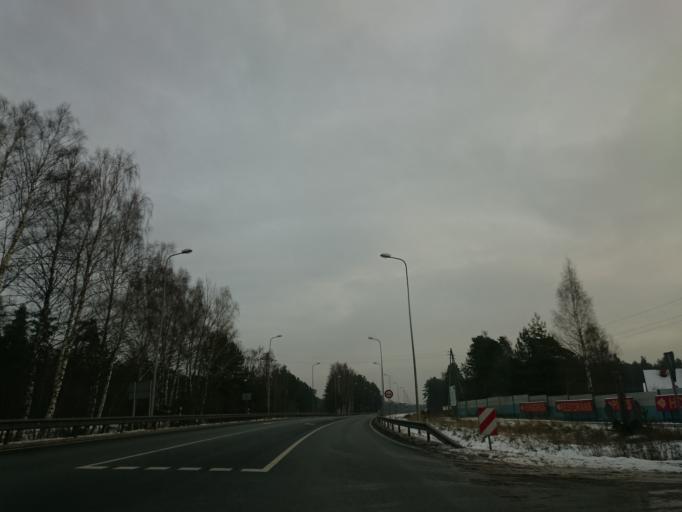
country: LV
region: Carnikava
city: Carnikava
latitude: 57.1903
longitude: 24.3492
